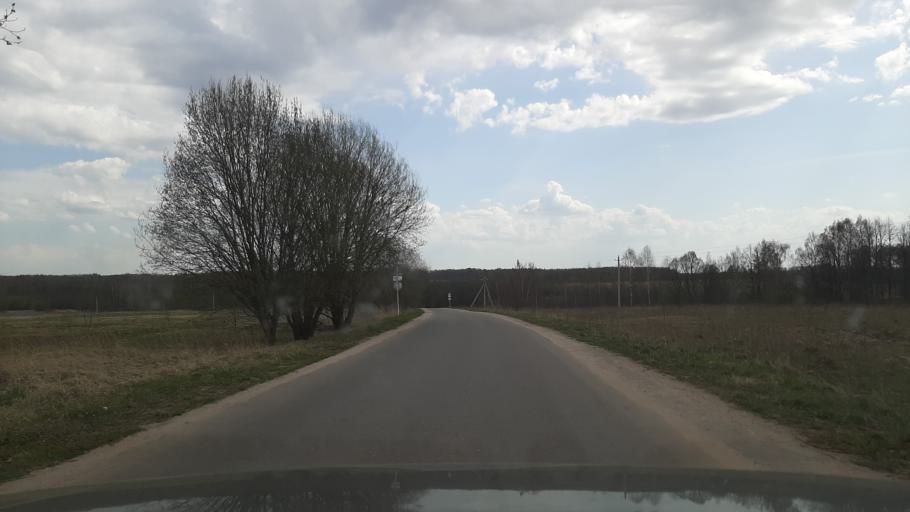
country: RU
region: Ivanovo
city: Furmanov
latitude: 57.3189
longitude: 41.1642
